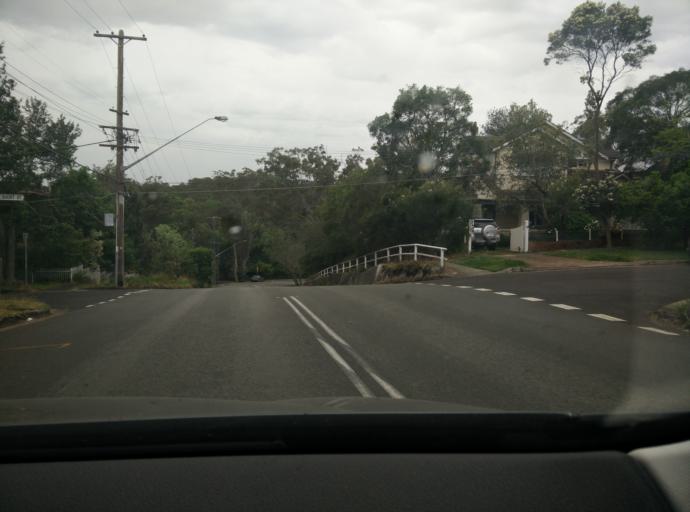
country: AU
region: New South Wales
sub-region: Ku-ring-gai
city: Lindfield
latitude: -33.7732
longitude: 151.1744
